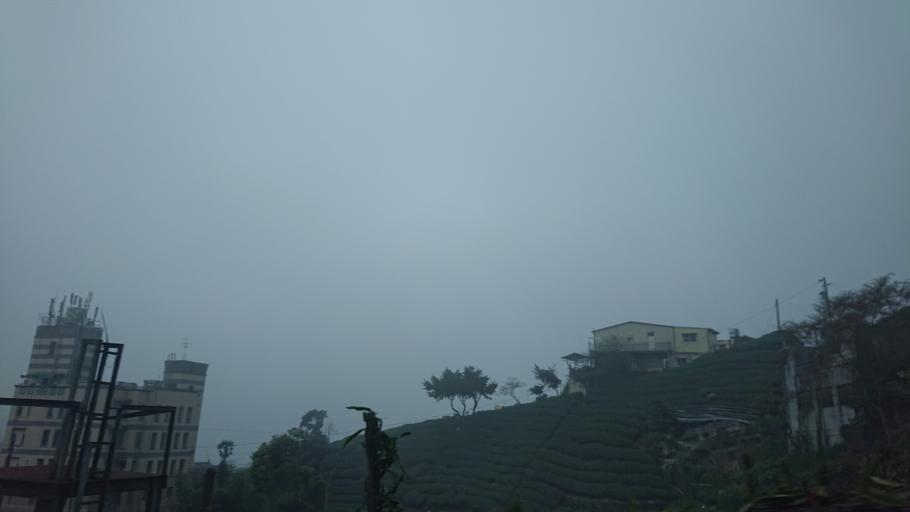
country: TW
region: Taiwan
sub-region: Chiayi
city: Jiayi Shi
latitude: 23.4745
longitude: 120.6986
